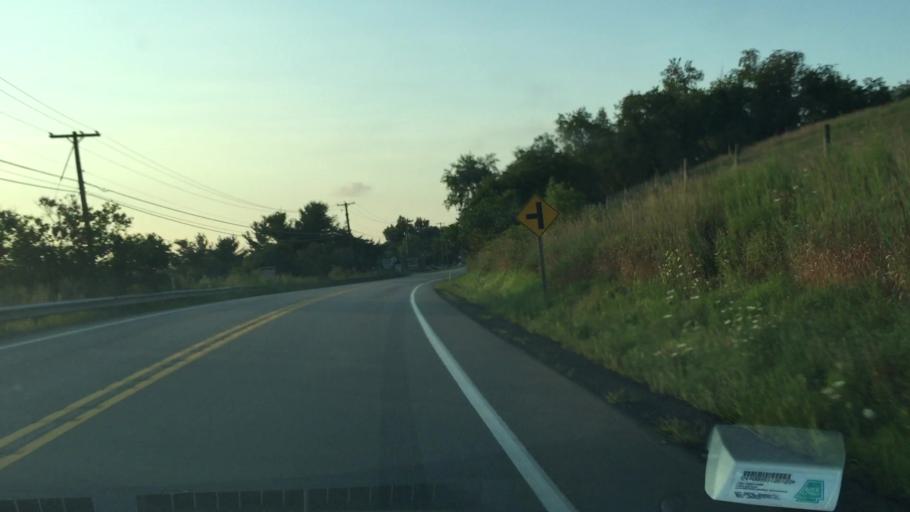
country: US
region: Pennsylvania
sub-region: Butler County
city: Mars
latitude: 40.7365
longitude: -80.0304
